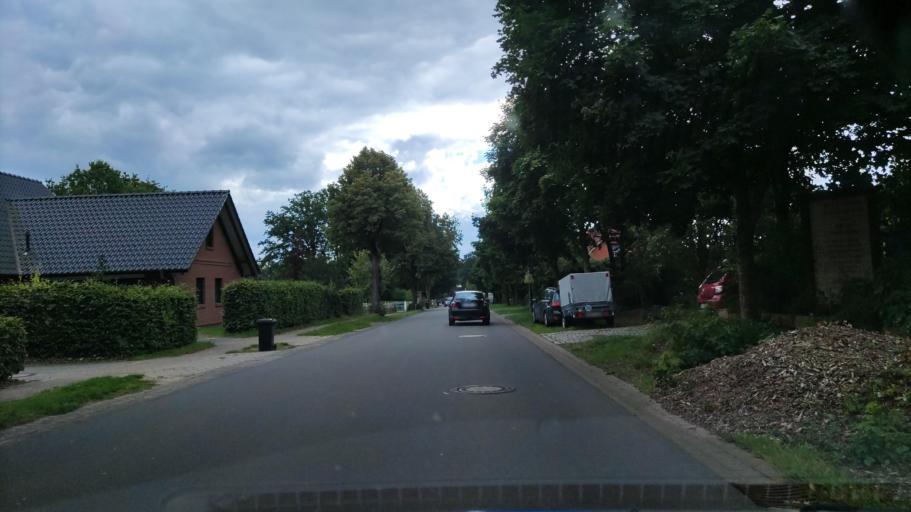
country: DE
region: Lower Saxony
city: Dohren
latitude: 53.3081
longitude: 9.7020
